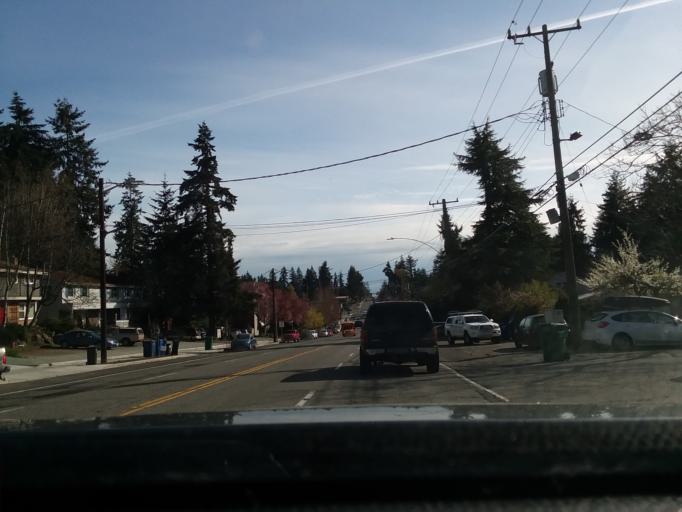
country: US
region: Washington
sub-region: King County
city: Shoreline
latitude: 47.7315
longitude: -122.3556
